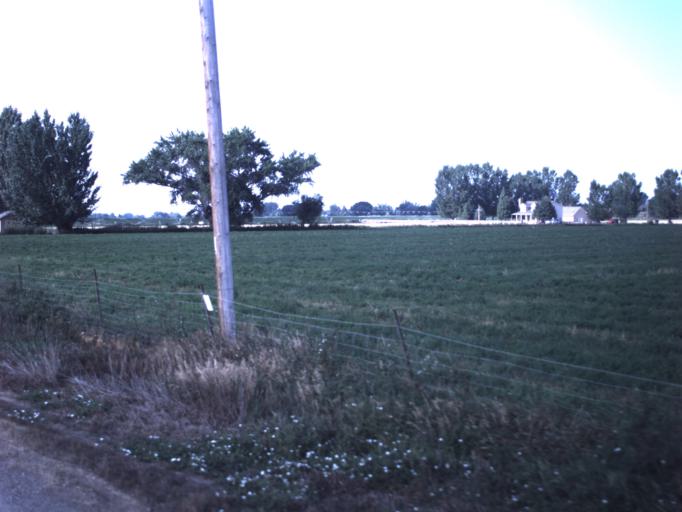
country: US
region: Utah
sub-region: Uintah County
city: Naples
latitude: 40.3856
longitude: -109.3459
